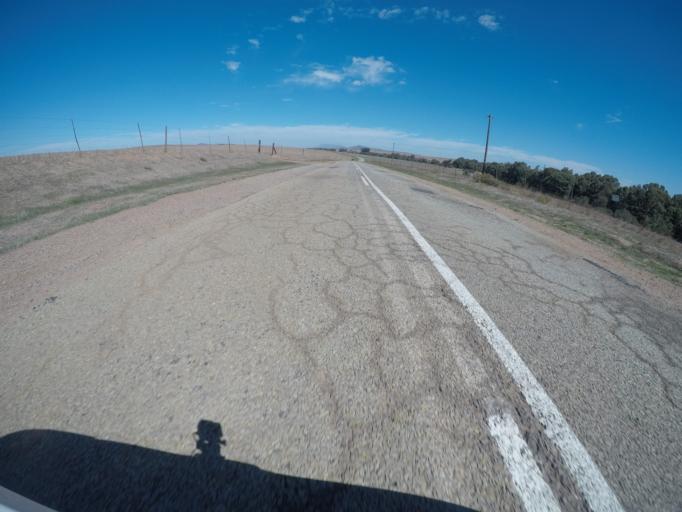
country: ZA
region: Western Cape
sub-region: City of Cape Town
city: Atlantis
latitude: -33.6161
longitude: 18.6349
